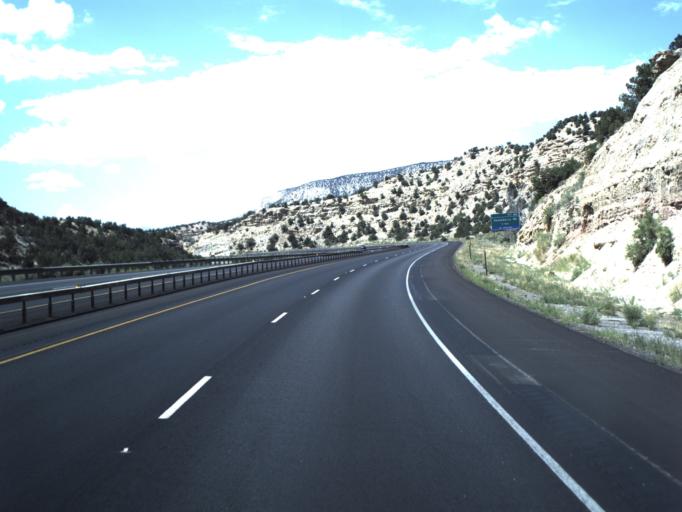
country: US
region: Utah
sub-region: Sevier County
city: Salina
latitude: 38.9133
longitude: -111.7162
